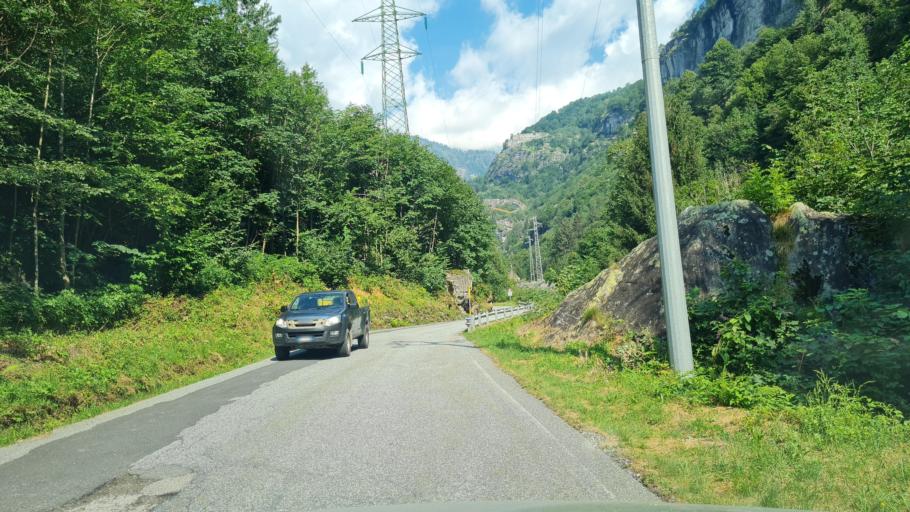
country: IT
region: Piedmont
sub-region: Provincia Verbano-Cusio-Ossola
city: Baceno
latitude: 46.2819
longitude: 8.2924
